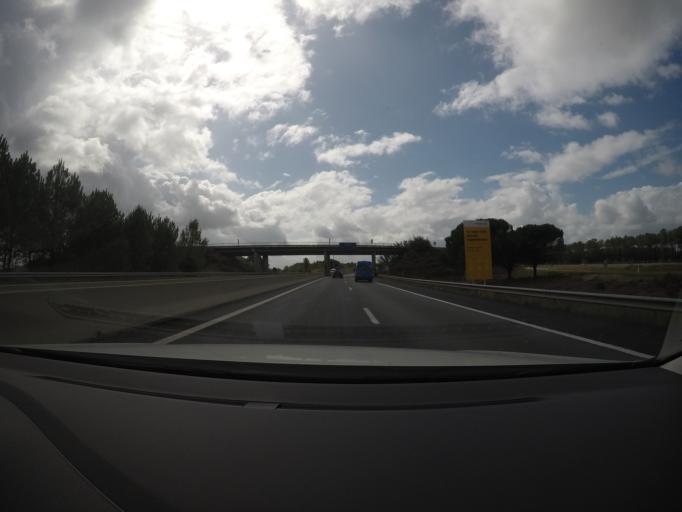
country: FR
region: Aquitaine
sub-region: Departement des Landes
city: Saint-Geours-de-Maremne
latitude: 43.6993
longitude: -1.2291
